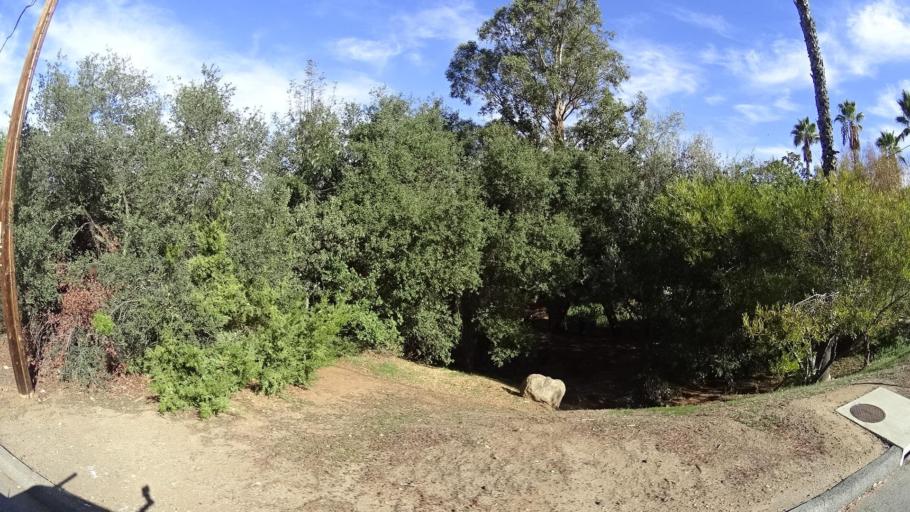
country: US
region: California
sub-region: San Diego County
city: Alpine
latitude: 32.8219
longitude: -116.7461
